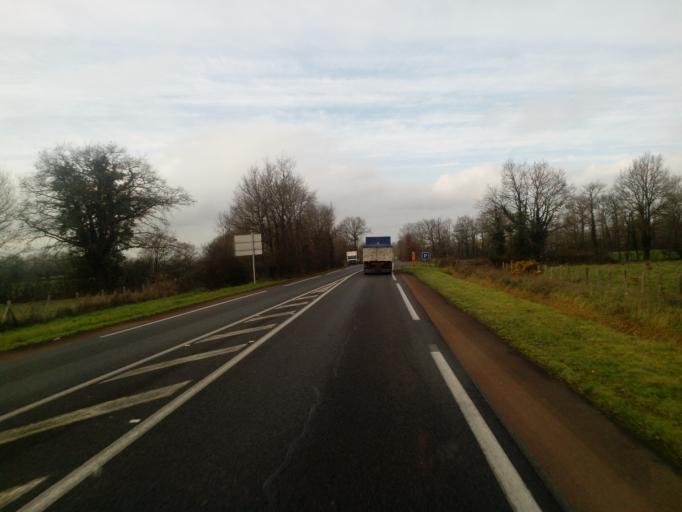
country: FR
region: Poitou-Charentes
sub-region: Departement des Deux-Sevres
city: Chiche
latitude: 46.7802
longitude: -0.3316
